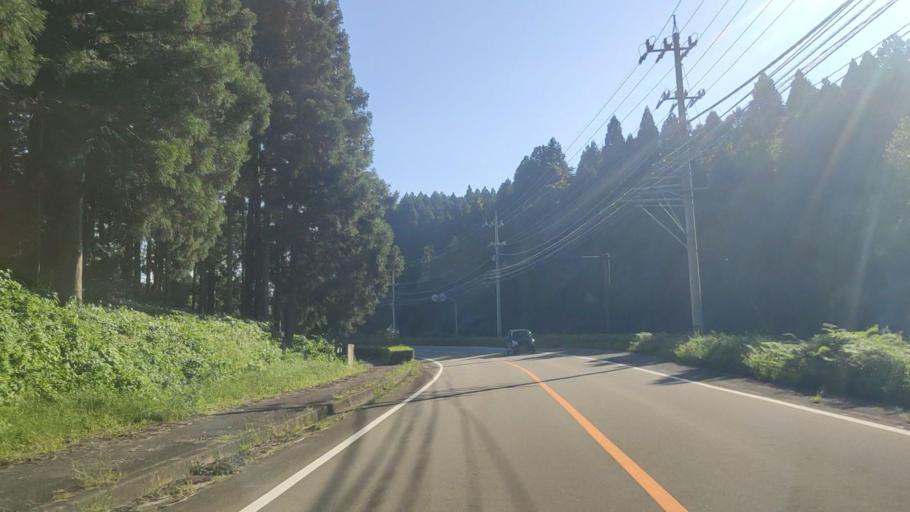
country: JP
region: Ishikawa
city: Nanao
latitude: 37.1204
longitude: 136.8620
